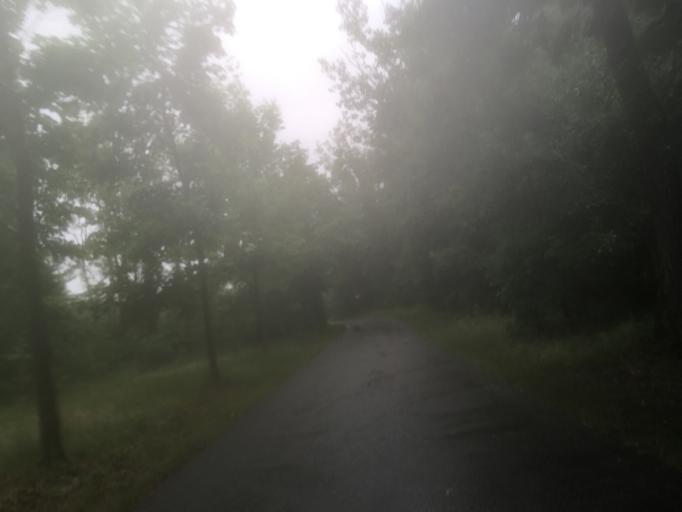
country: DE
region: Brandenburg
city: Zehdenick
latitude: 53.0155
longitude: 13.3118
